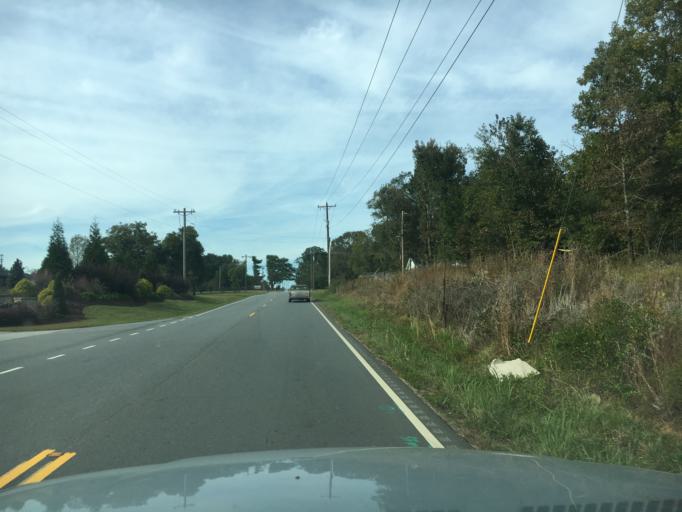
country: US
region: South Carolina
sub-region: Spartanburg County
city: Duncan
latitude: 34.8695
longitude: -82.1173
